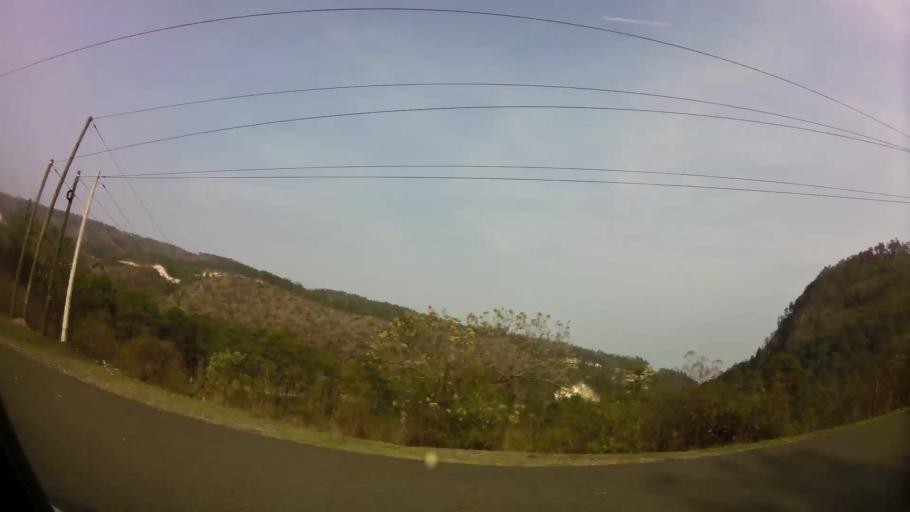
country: HN
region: Francisco Morazan
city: Zambrano
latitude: 14.2887
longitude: -87.4738
